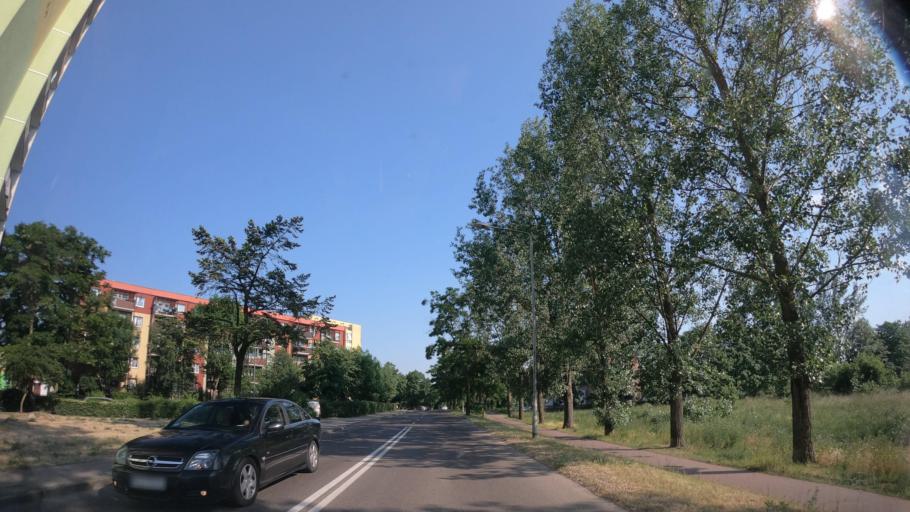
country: PL
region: West Pomeranian Voivodeship
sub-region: Powiat stargardzki
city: Stargard Szczecinski
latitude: 53.3398
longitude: 15.0034
